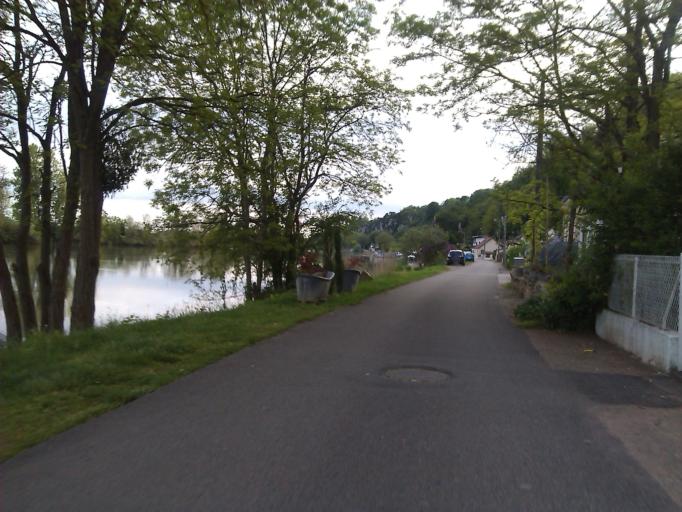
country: FR
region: Franche-Comte
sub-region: Departement du Jura
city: Dole
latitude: 47.1319
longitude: 5.5742
